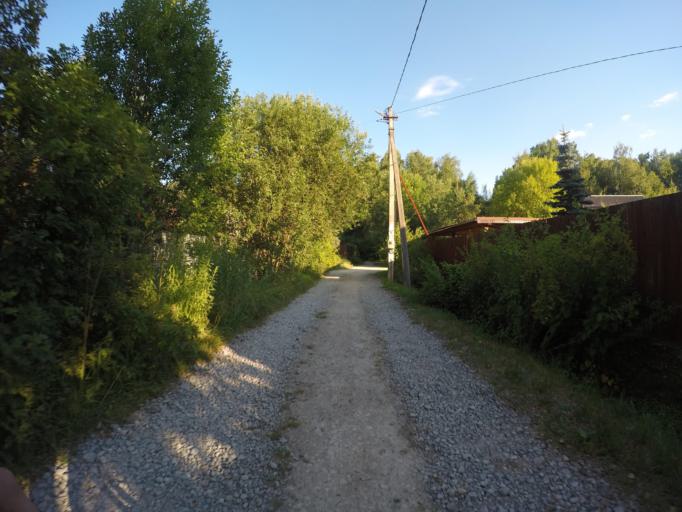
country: RU
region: Moskovskaya
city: Rechitsy
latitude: 55.6052
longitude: 38.4977
